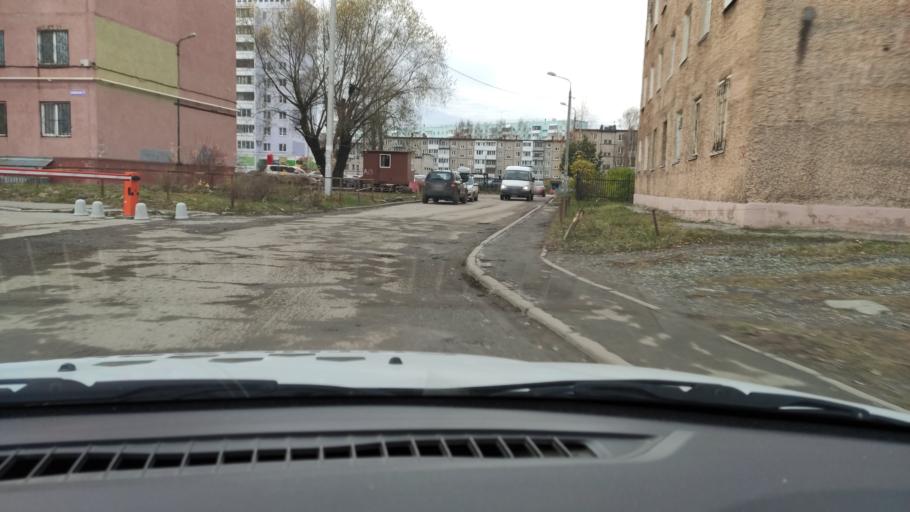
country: RU
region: Perm
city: Perm
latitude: 57.9699
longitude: 56.1941
